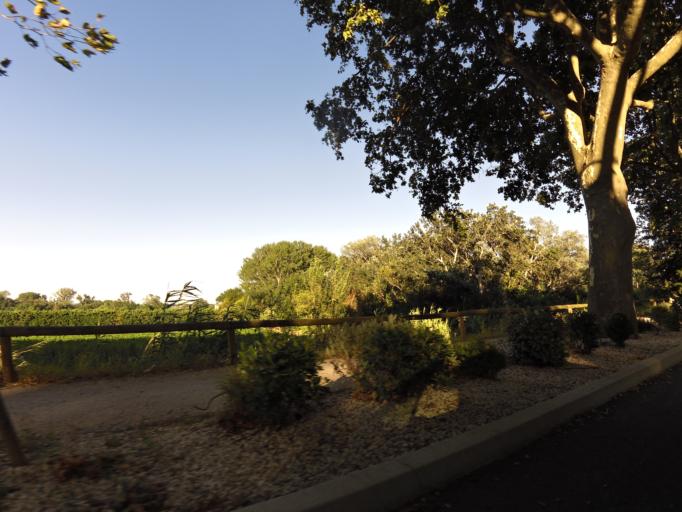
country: FR
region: Languedoc-Roussillon
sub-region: Departement du Gard
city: Remoulins
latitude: 43.9397
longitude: 4.5537
